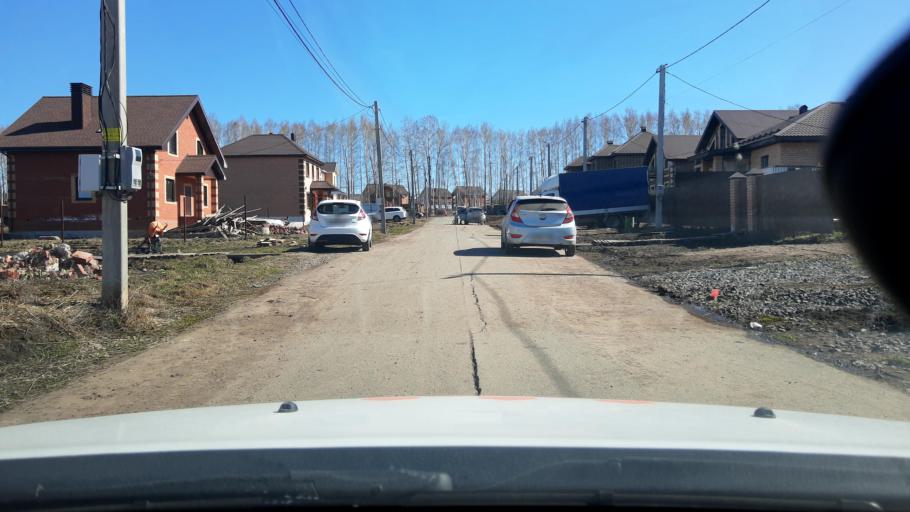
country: RU
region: Bashkortostan
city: Kabakovo
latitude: 54.6156
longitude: 56.1153
